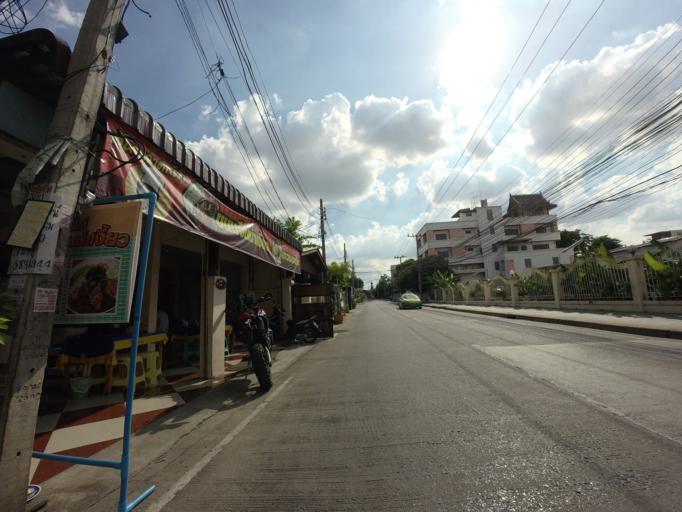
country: TH
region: Bangkok
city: Huai Khwang
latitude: 13.7819
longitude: 100.5938
